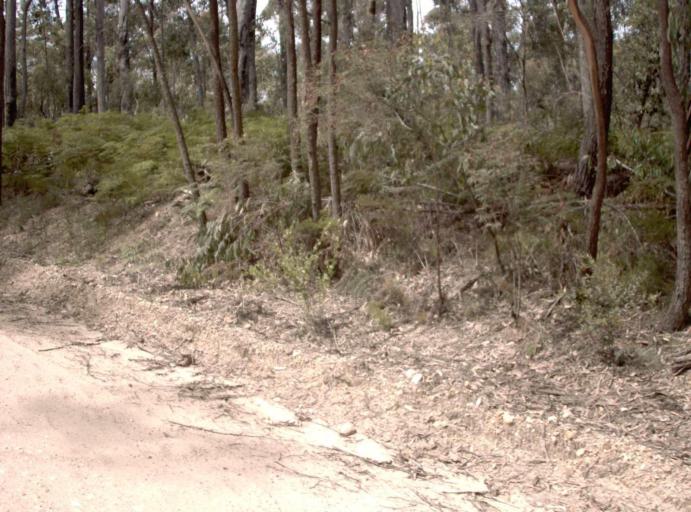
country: AU
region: Victoria
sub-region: East Gippsland
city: Lakes Entrance
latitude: -37.6686
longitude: 148.6325
